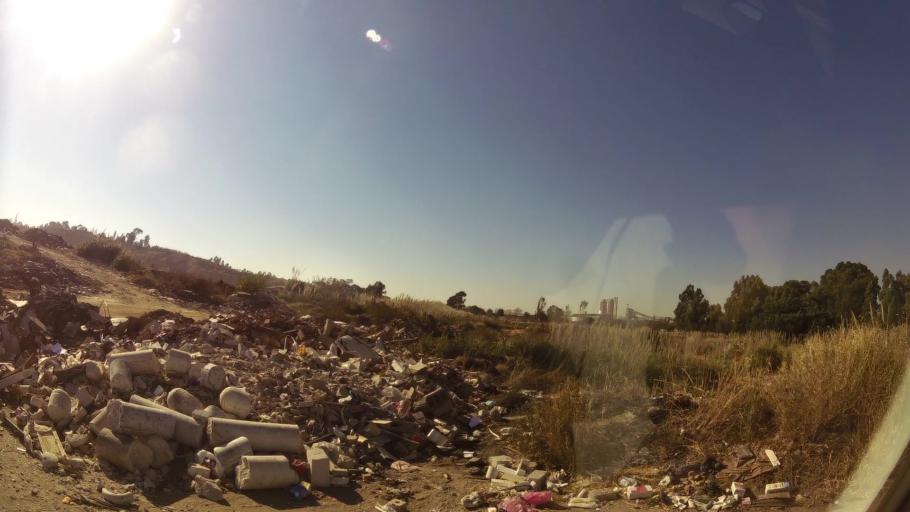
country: ZA
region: Gauteng
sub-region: Ekurhuleni Metropolitan Municipality
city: Germiston
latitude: -26.2192
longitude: 28.1149
